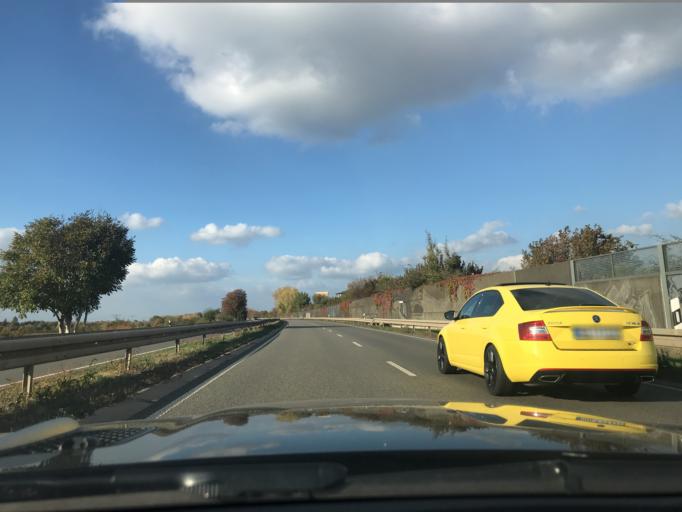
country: DE
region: Thuringia
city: Erfurt
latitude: 50.9976
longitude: 11.0010
